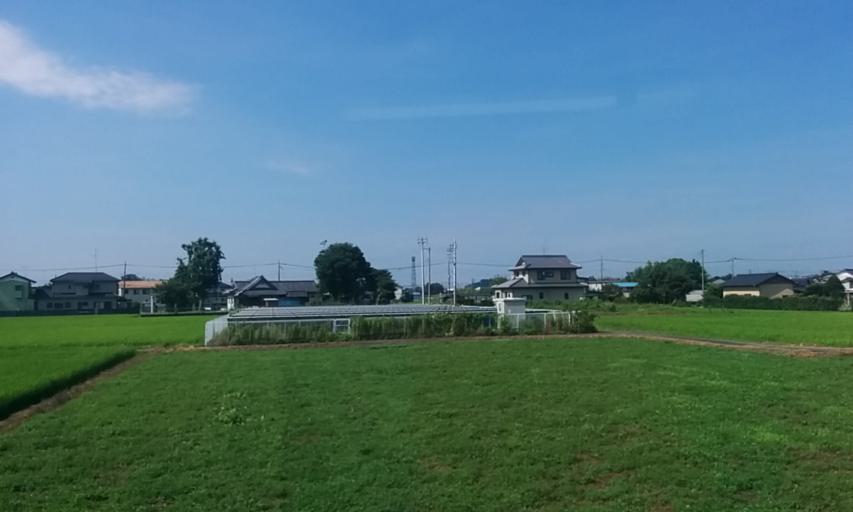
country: JP
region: Saitama
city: Hanyu
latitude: 36.1564
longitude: 139.5472
